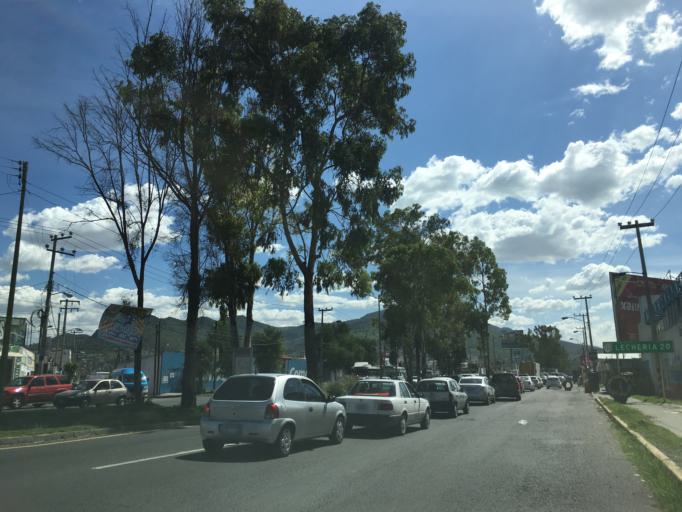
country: MX
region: Mexico
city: Ecatepec
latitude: 19.6139
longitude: -99.0424
